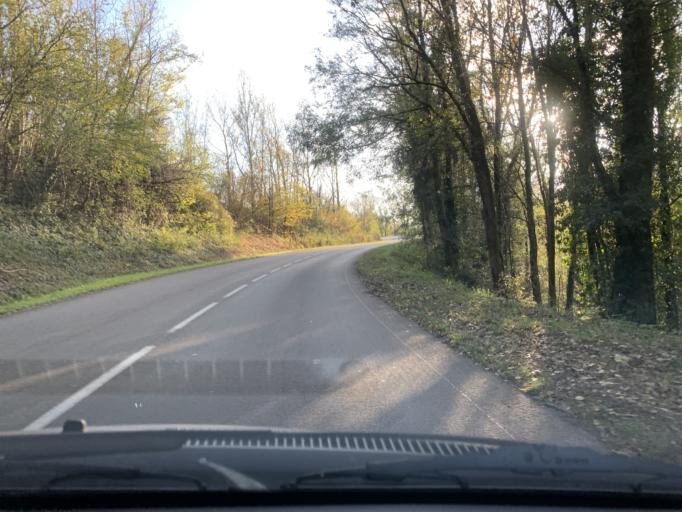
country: FR
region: Rhone-Alpes
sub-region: Departement de la Drome
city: Saint-Jean-en-Royans
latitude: 45.0411
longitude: 5.3032
